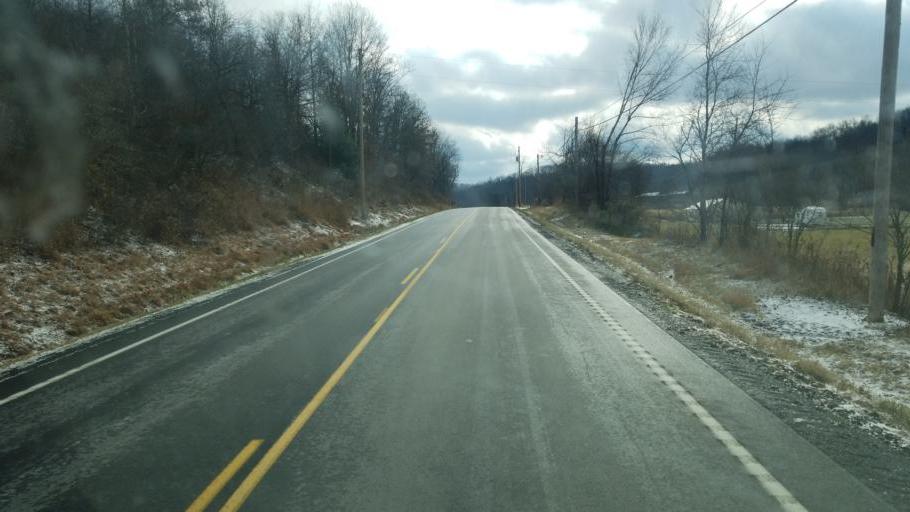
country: US
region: Ohio
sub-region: Muskingum County
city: Frazeysburg
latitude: 40.1286
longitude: -82.1957
